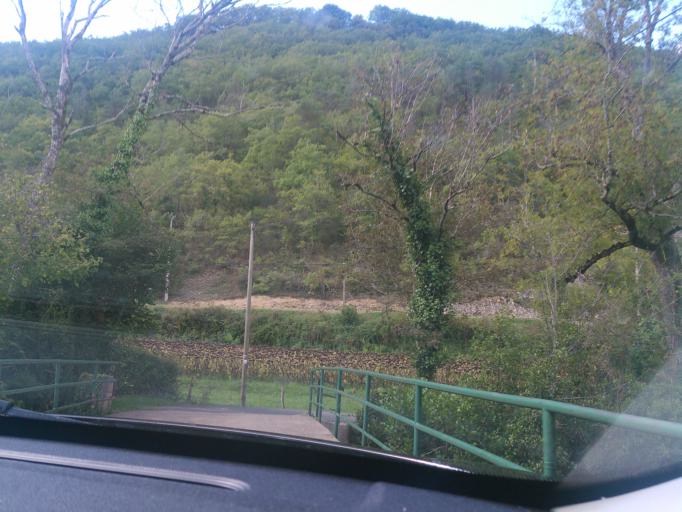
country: FR
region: Aquitaine
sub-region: Departement de la Dordogne
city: Cenac-et-Saint-Julien
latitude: 44.8086
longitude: 1.1546
